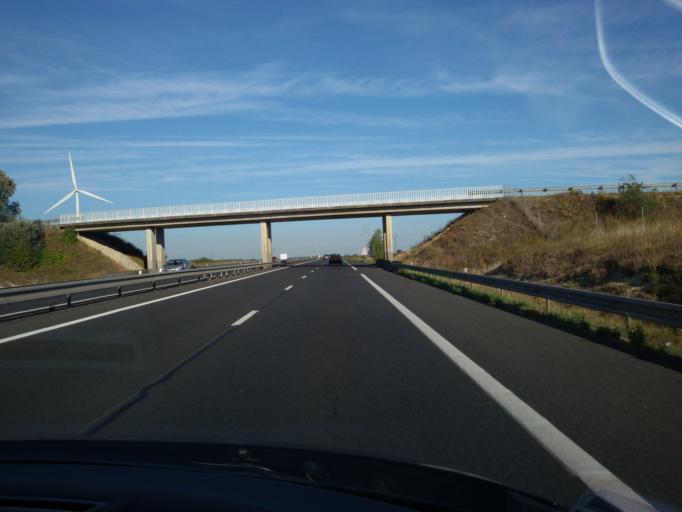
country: FR
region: Centre
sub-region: Departement du Cher
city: Mehun-sur-Yevre
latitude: 47.0993
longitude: 2.2300
